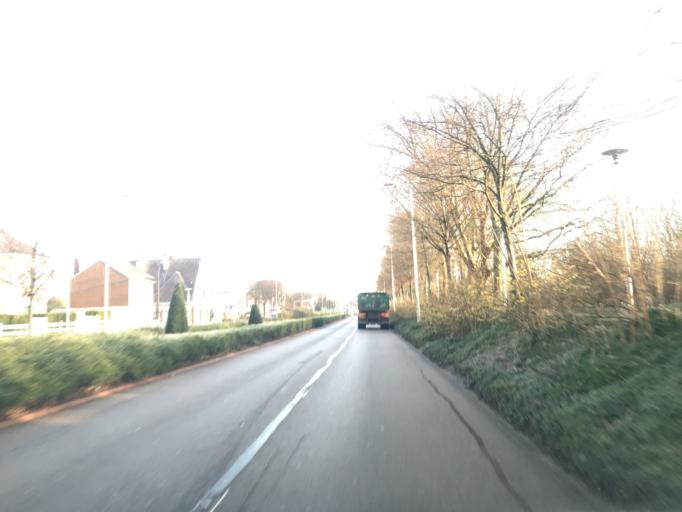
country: FR
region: Haute-Normandie
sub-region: Departement de la Seine-Maritime
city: Le Petit-Quevilly
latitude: 49.4074
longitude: 1.0694
